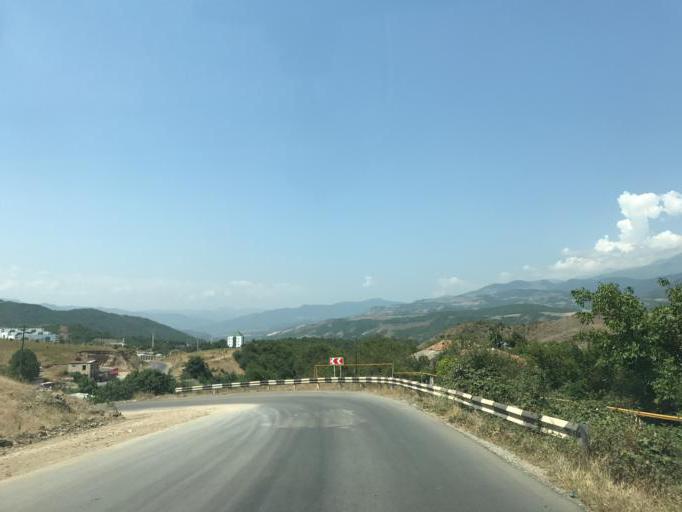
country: AZ
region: Tartar Rayon
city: Martakert
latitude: 40.1468
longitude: 46.6051
